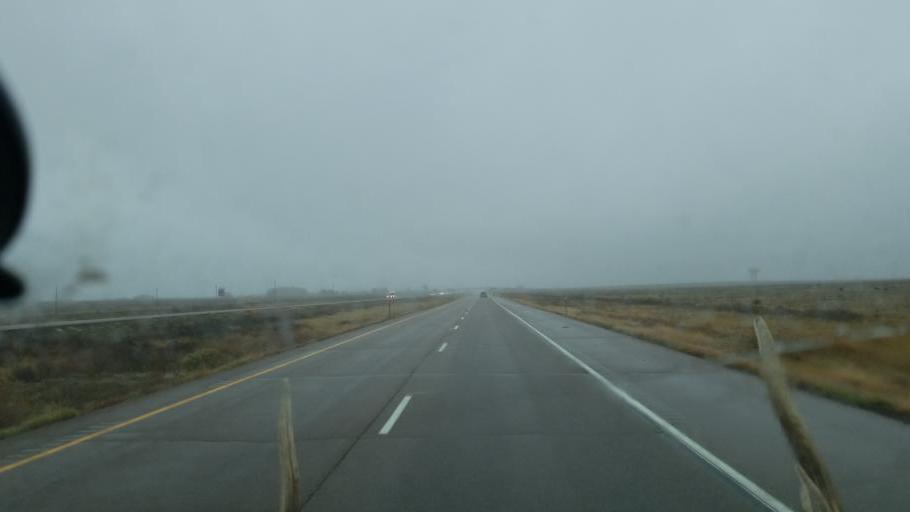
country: US
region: Colorado
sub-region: Pueblo County
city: Pueblo
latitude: 38.1505
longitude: -104.6528
